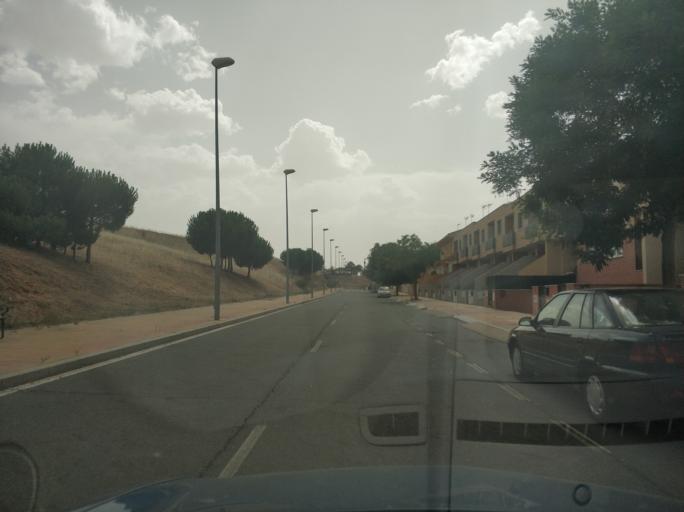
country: ES
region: Castille and Leon
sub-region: Provincia de Salamanca
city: Salamanca
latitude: 40.9523
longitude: -5.6862
